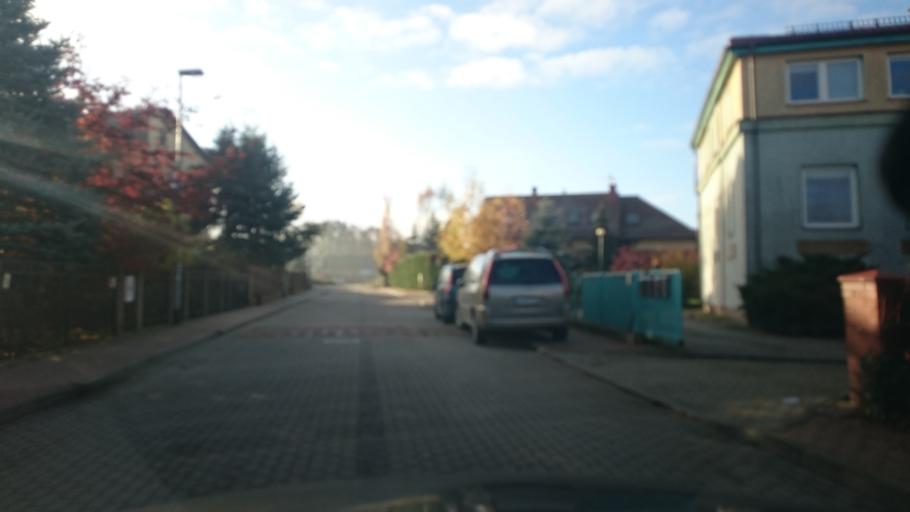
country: PL
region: Pomeranian Voivodeship
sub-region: Gdynia
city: Wielki Kack
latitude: 54.4624
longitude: 18.4933
